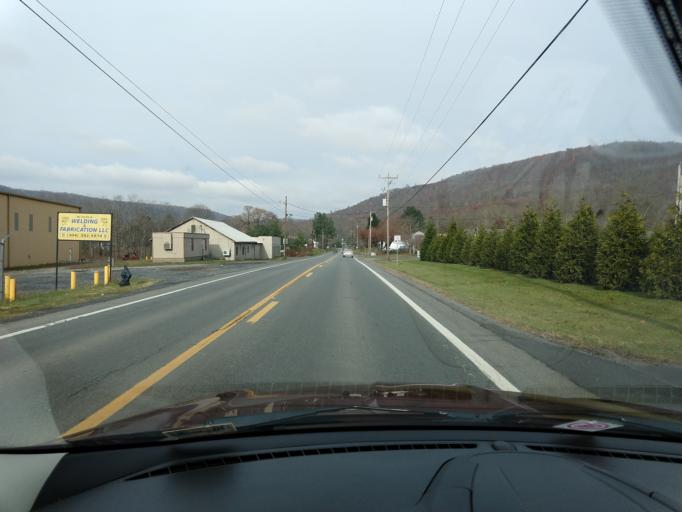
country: US
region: West Virginia
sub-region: Greenbrier County
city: Rainelle
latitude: 37.9806
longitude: -80.7144
